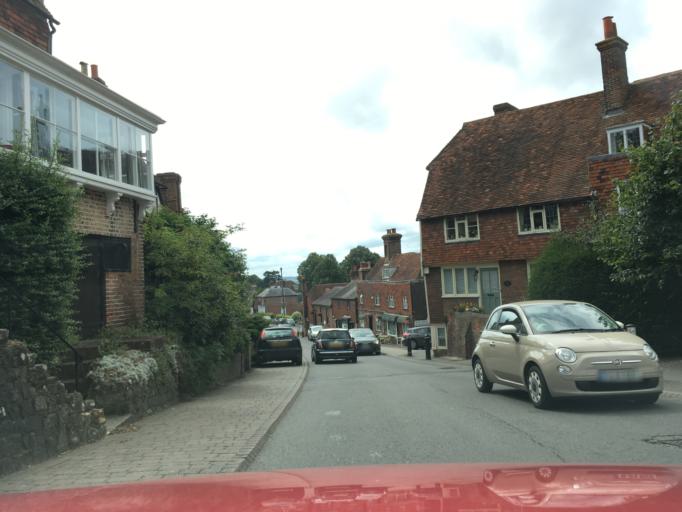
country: GB
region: England
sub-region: Kent
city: Marden
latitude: 51.1135
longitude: 0.4603
